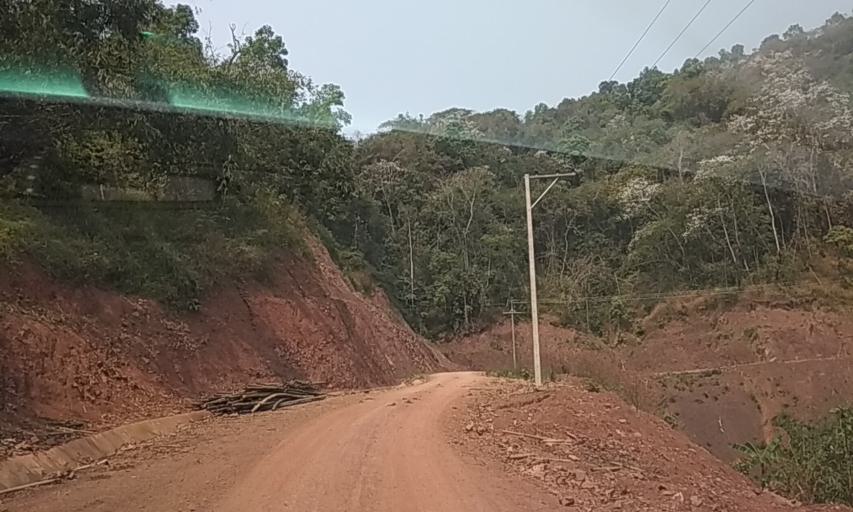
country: VN
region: Huyen Dien Bien
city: Dien Bien Phu
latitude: 21.4545
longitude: 102.7669
